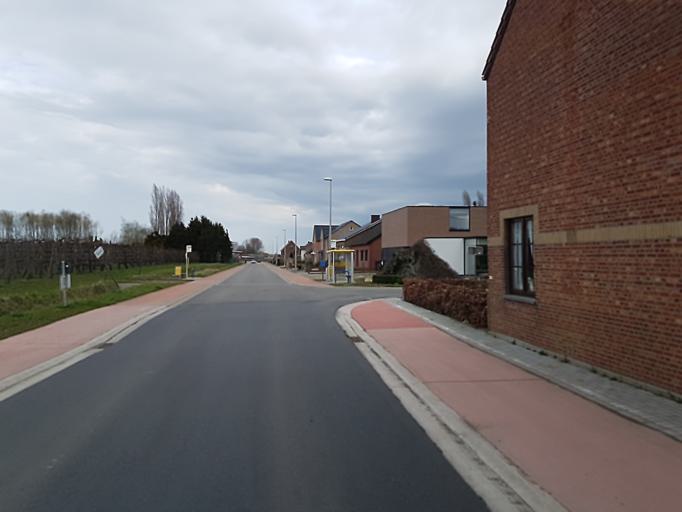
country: BE
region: Flanders
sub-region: Provincie Limburg
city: Nieuwerkerken
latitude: 50.9032
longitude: 5.2349
